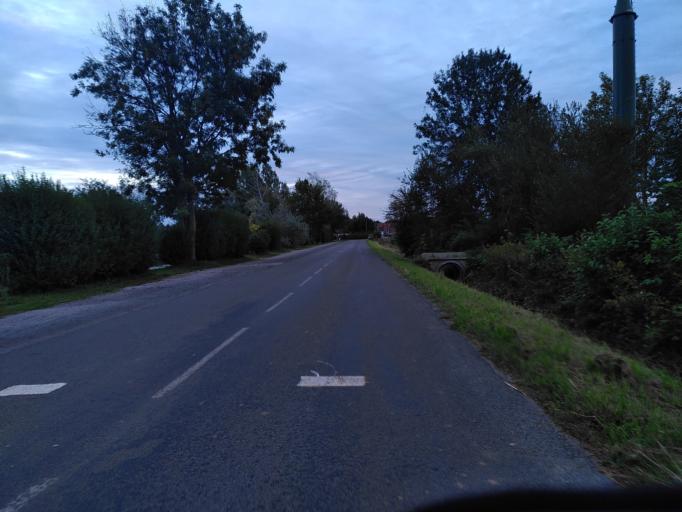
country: FR
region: Nord-Pas-de-Calais
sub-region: Departement du Pas-de-Calais
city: Mametz
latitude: 50.6403
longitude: 2.2982
